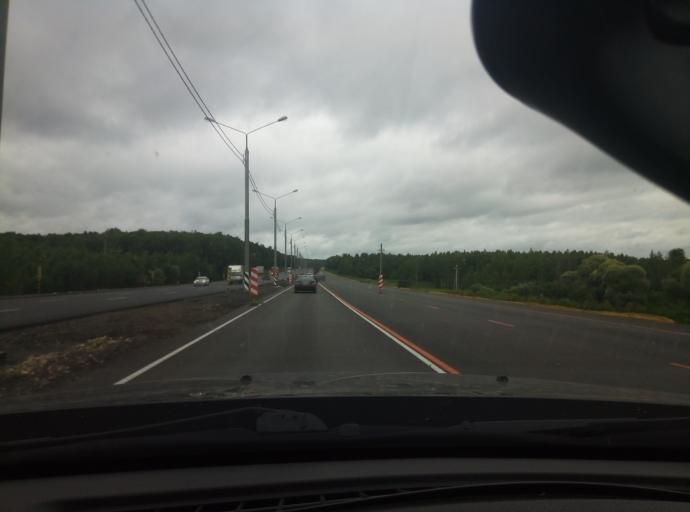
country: RU
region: Tula
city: Zaokskiy
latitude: 54.6038
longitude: 37.4986
